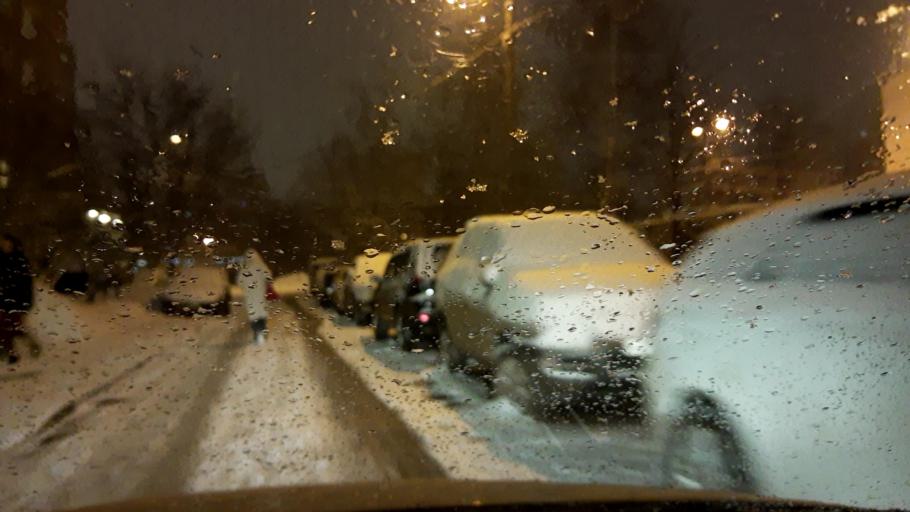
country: RU
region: Moskovskaya
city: Shcherbinka
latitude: 55.5409
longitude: 37.5763
